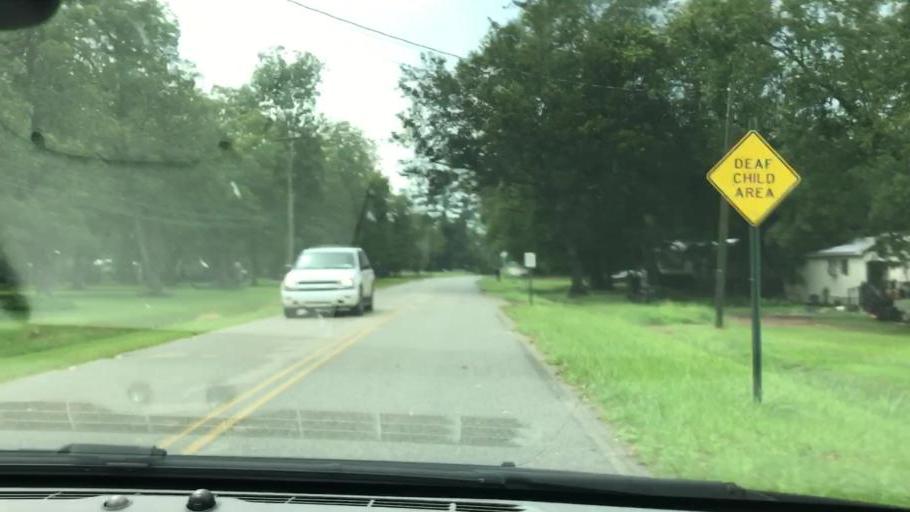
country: US
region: Georgia
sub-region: Early County
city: Blakely
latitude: 31.3746
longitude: -84.9467
